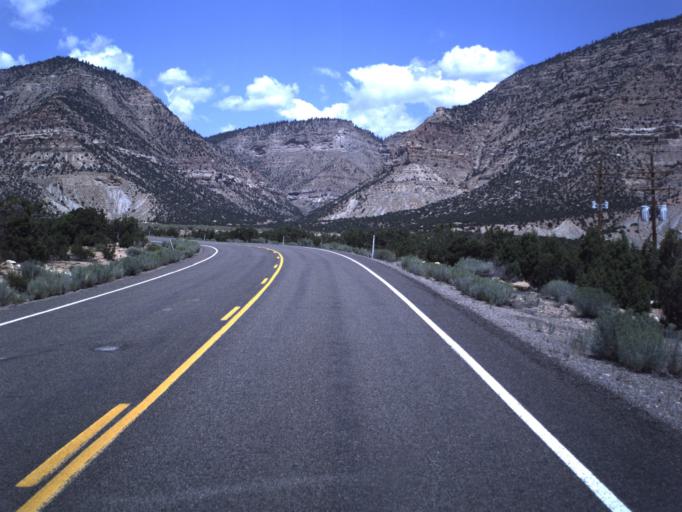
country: US
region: Utah
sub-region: Emery County
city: Orangeville
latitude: 39.2934
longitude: -111.1111
